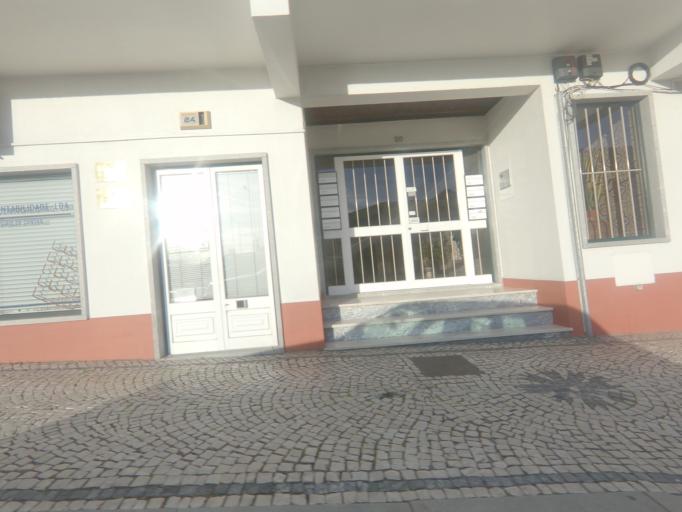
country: PT
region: Castelo Branco
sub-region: Castelo Branco
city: Castelo Branco
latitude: 39.8215
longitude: -7.4893
